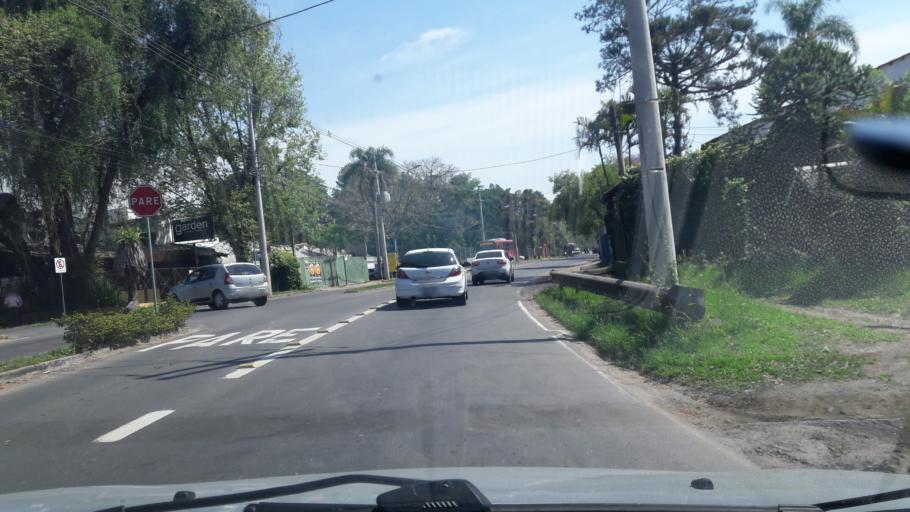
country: BR
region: Rio Grande do Sul
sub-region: Guaiba
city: Guaiba
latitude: -30.1304
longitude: -51.2379
